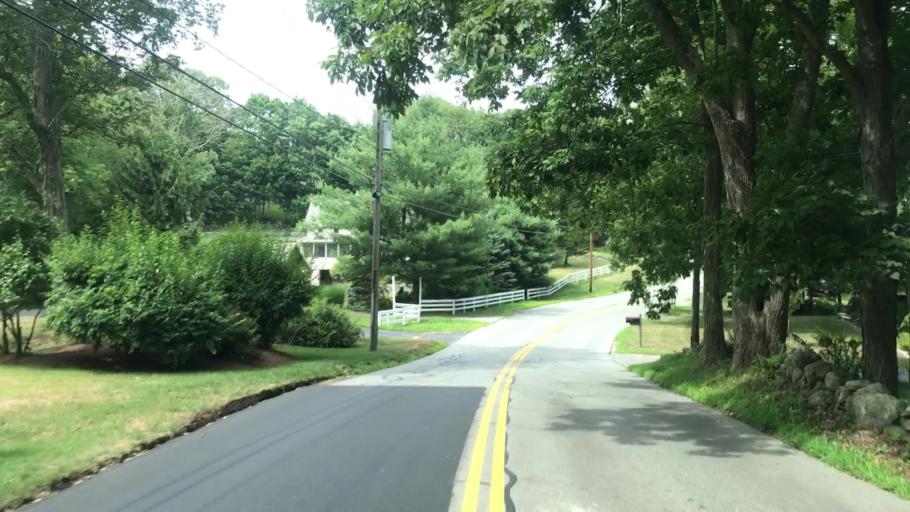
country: US
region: Connecticut
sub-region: New London County
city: Niantic
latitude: 41.3415
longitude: -72.2166
